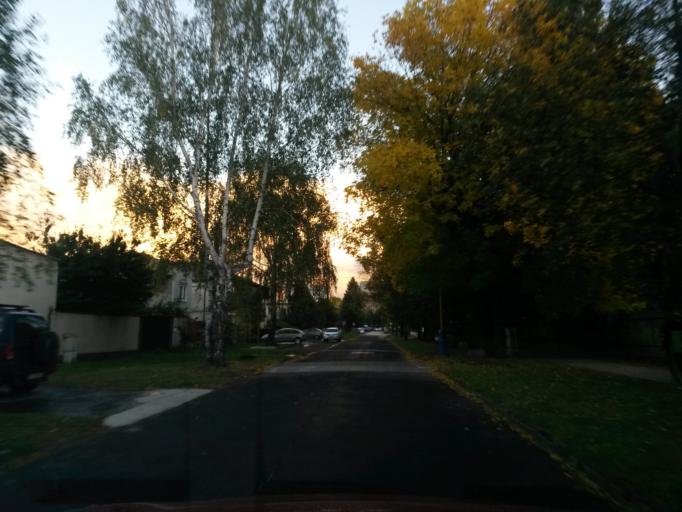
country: SK
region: Kosicky
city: Kosice
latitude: 48.6890
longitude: 21.2872
